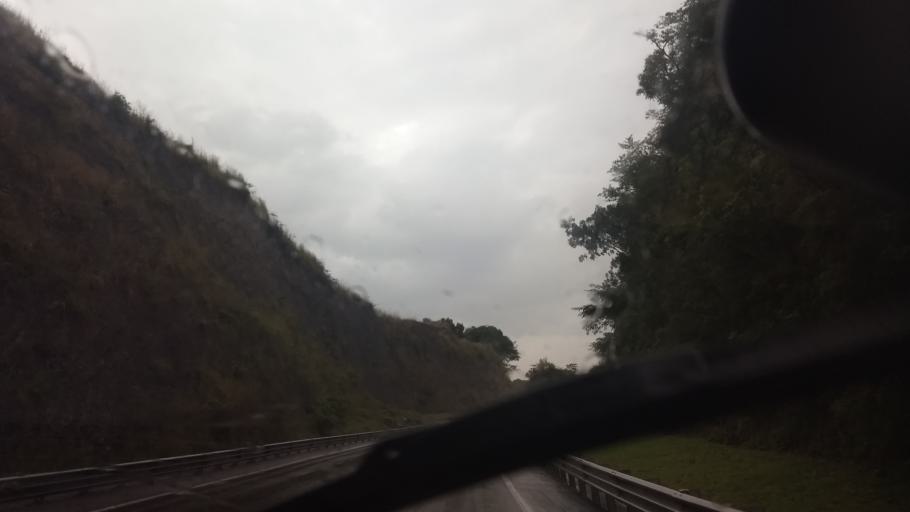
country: MX
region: Jalisco
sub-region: Tonila
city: San Marcos
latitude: 19.4490
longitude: -103.4740
